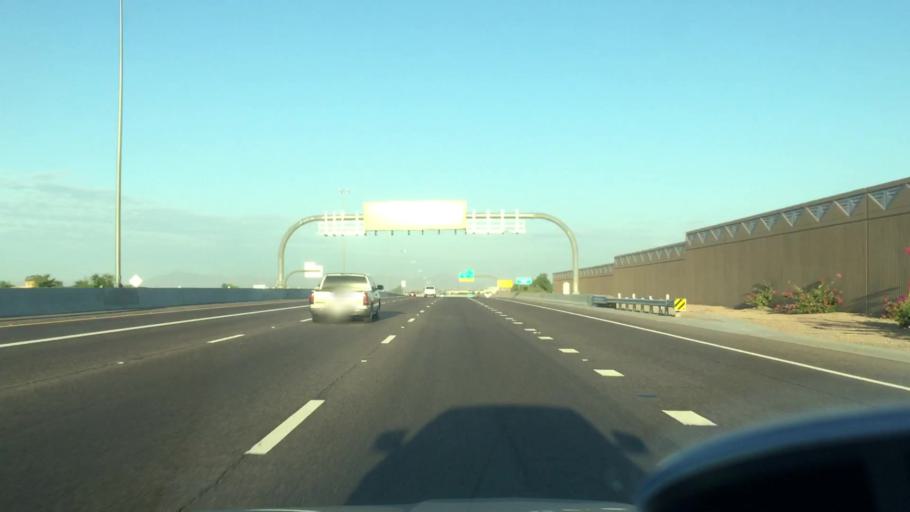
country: US
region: Arizona
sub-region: Maricopa County
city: Chandler
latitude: 33.2829
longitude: -111.8133
